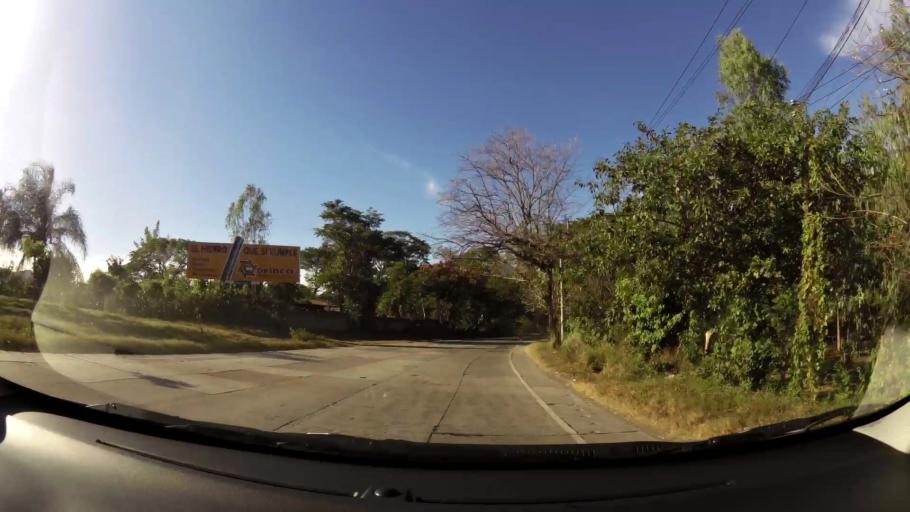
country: SV
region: Santa Ana
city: Texistepeque
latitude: 14.1342
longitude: -89.5071
